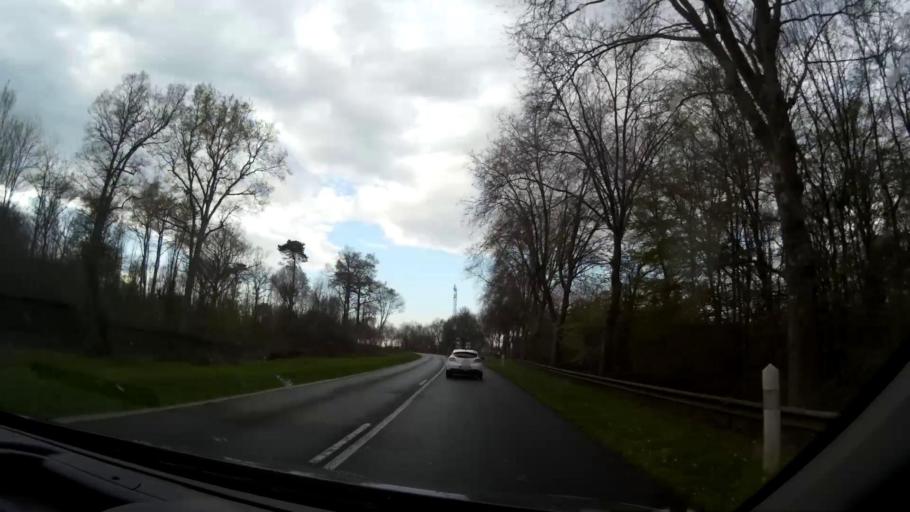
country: FR
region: Centre
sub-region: Departement du Loir-et-Cher
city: Cormeray
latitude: 47.4685
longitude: 1.4244
